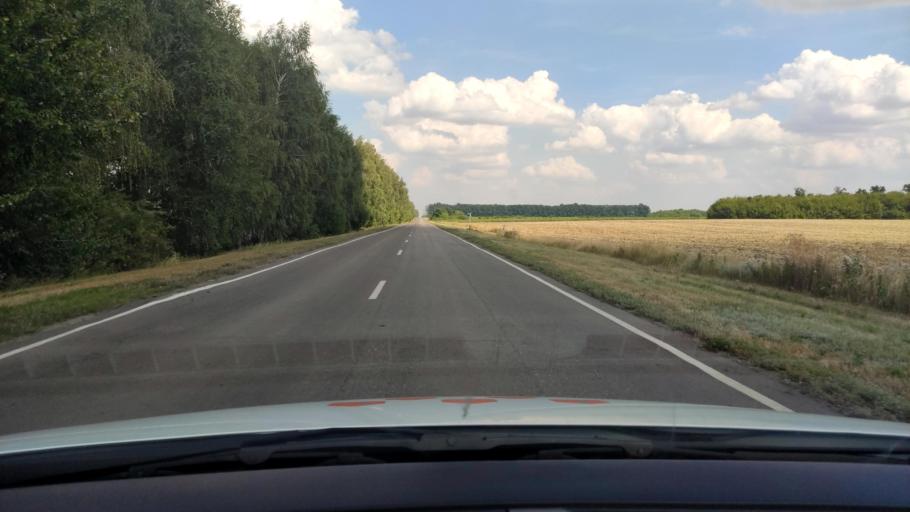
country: RU
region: Voronezj
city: Ertil'
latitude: 51.7926
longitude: 40.6906
